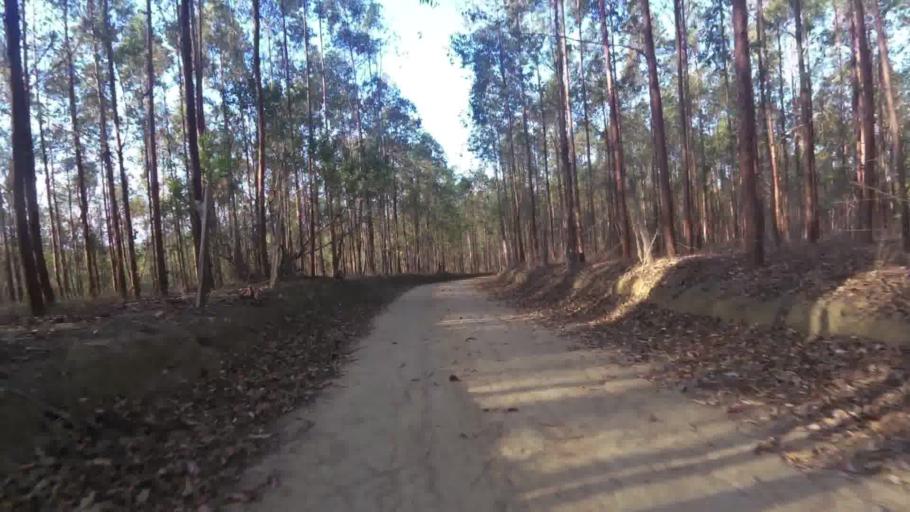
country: BR
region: Espirito Santo
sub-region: Marataizes
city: Marataizes
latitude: -21.1635
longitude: -41.0417
